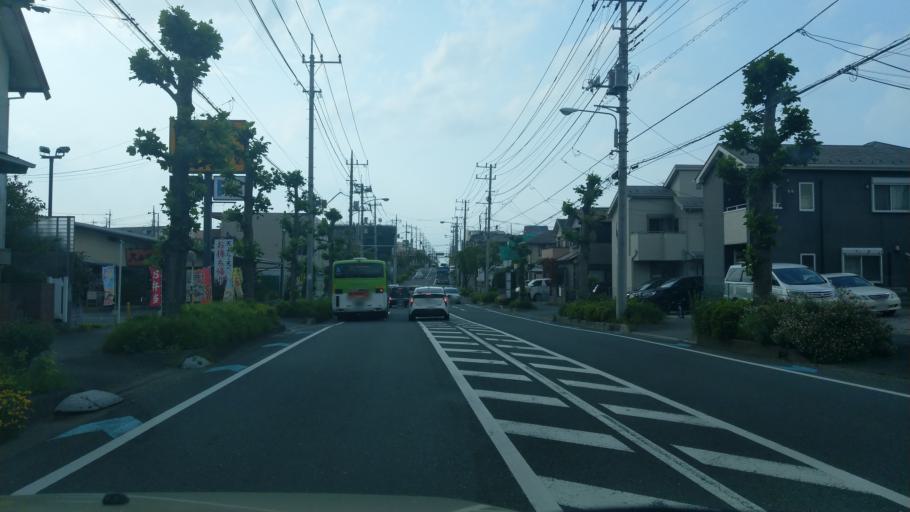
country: JP
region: Saitama
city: Saitama
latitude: 35.8812
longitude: 139.6903
